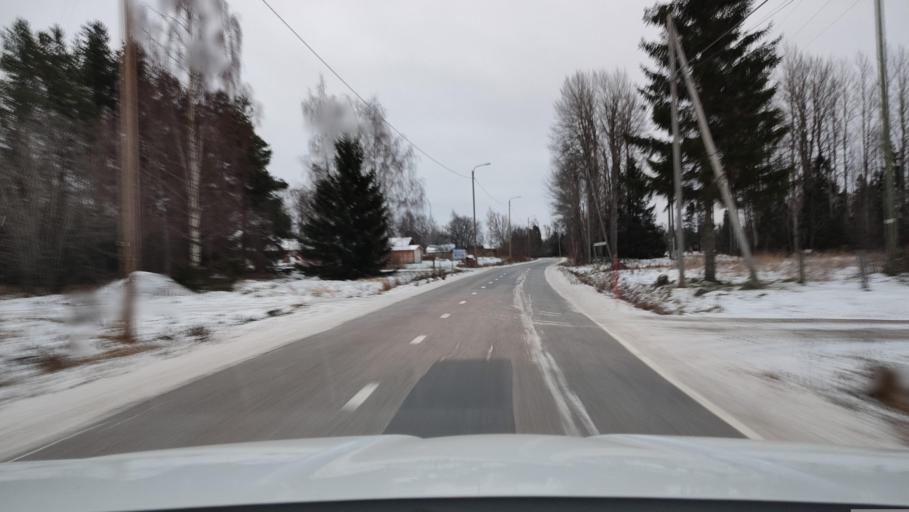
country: FI
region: Ostrobothnia
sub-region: Vaasa
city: Replot
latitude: 63.3491
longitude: 21.3030
